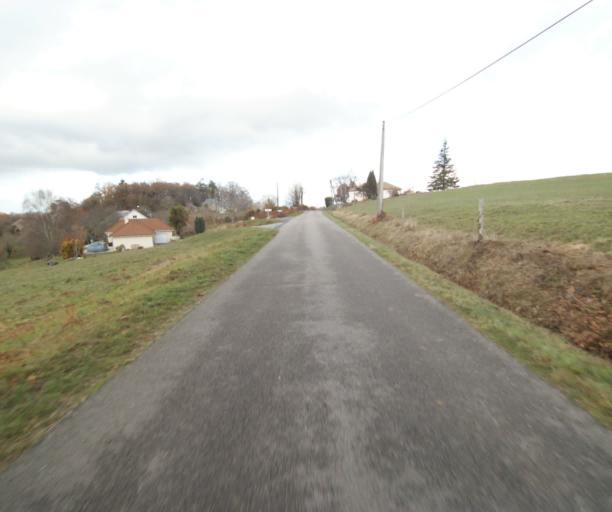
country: FR
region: Limousin
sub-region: Departement de la Correze
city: Sainte-Fortunade
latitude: 45.2141
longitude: 1.7895
